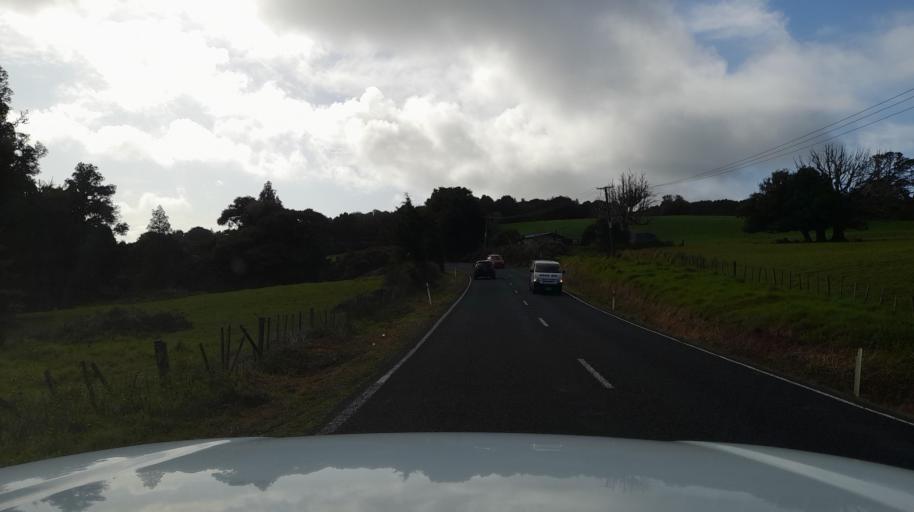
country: NZ
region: Northland
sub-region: Far North District
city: Waimate North
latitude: -35.3621
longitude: 173.8166
